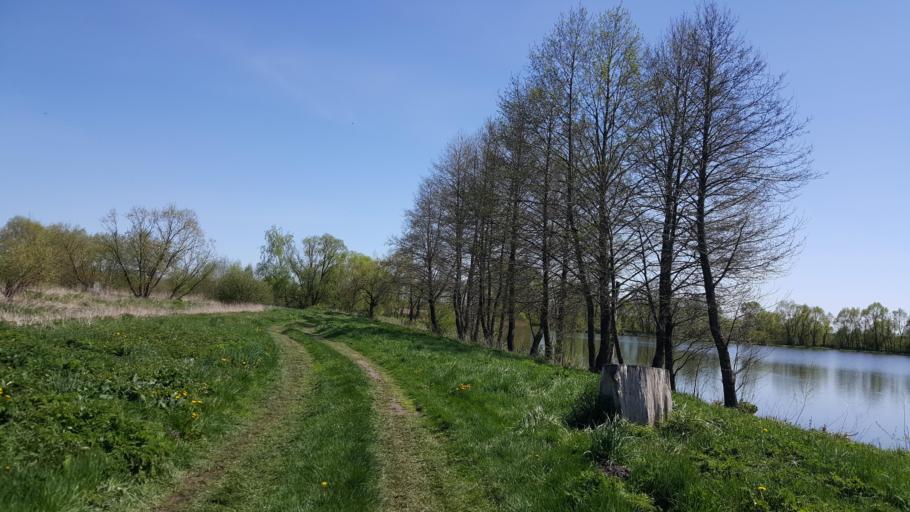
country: BY
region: Brest
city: Kamyanyets
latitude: 52.4366
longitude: 23.8504
